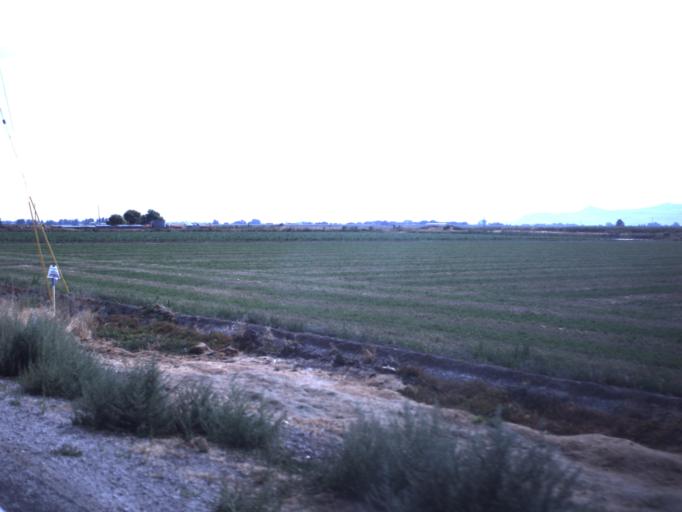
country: US
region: Utah
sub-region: Box Elder County
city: Honeyville
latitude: 41.6747
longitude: -112.0898
